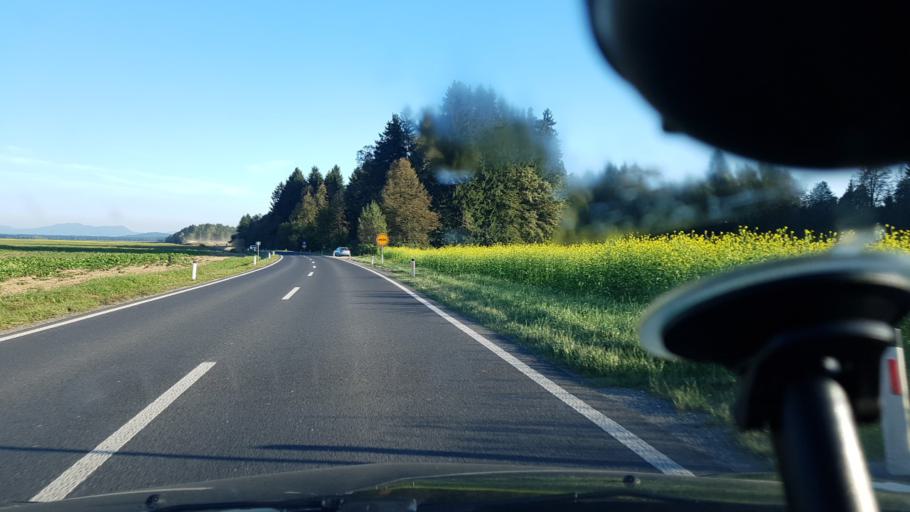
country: SI
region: Sencur
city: Sencur
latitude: 46.2314
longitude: 14.4346
